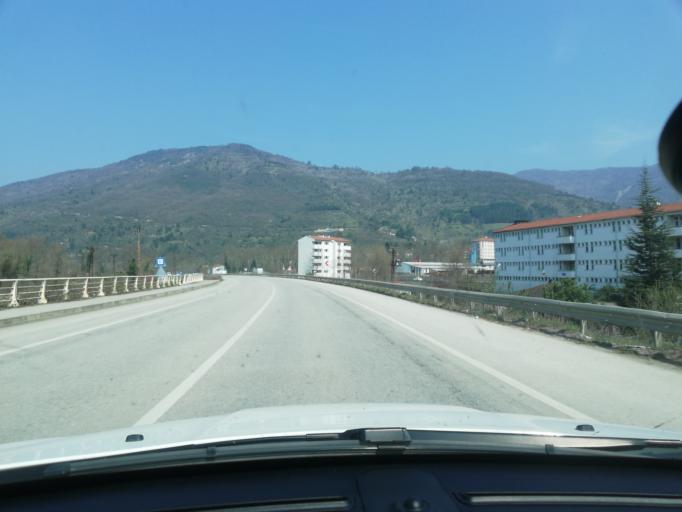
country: TR
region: Karabuk
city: Yenice
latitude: 41.2136
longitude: 32.3091
